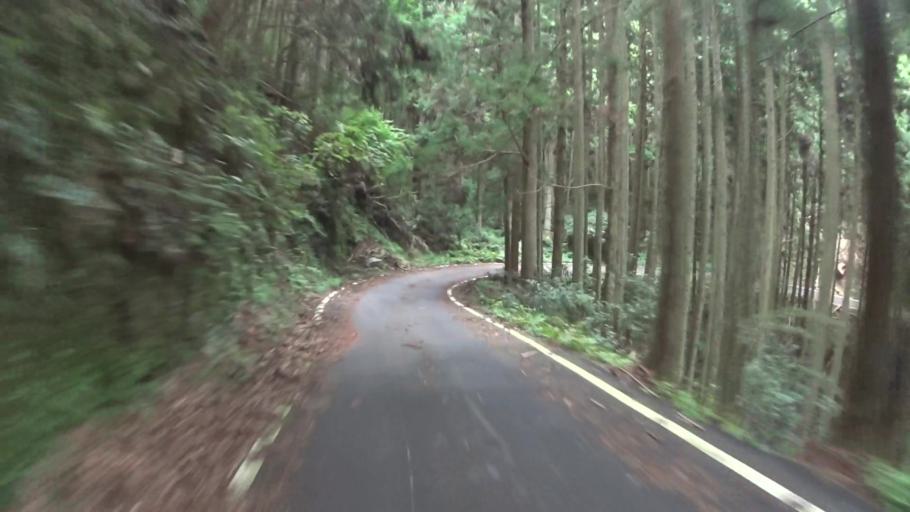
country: JP
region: Kyoto
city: Uji
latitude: 34.8499
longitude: 135.9456
